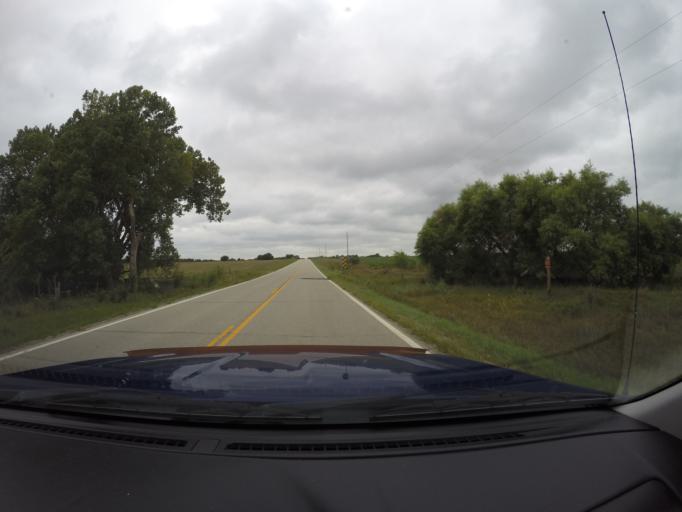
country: US
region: Kansas
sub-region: Morris County
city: Council Grove
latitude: 38.7977
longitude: -96.6741
